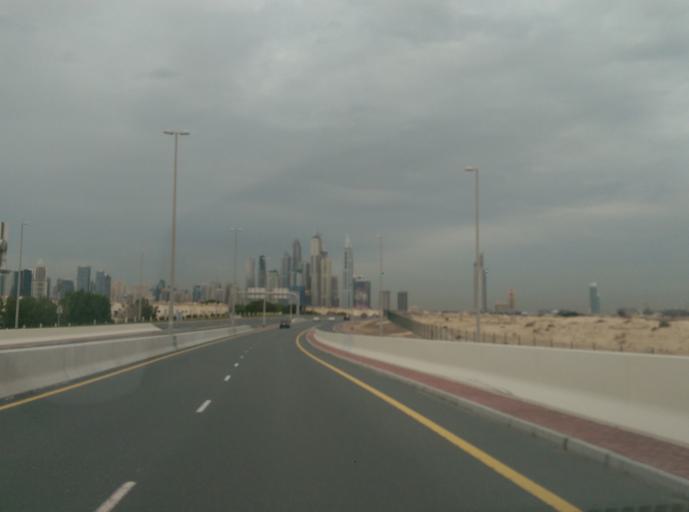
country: AE
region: Dubai
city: Dubai
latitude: 25.0799
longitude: 55.1778
